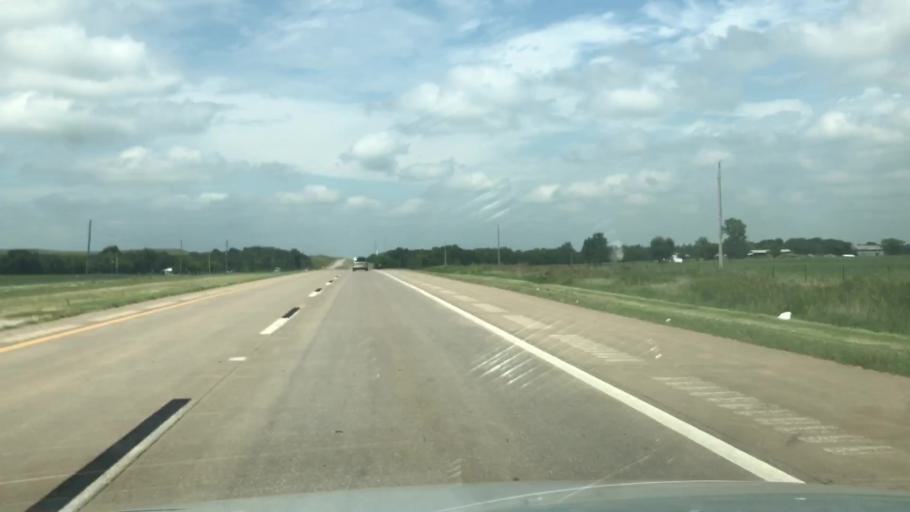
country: US
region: Oklahoma
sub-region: Osage County
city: Skiatook
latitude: 36.4636
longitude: -95.9204
